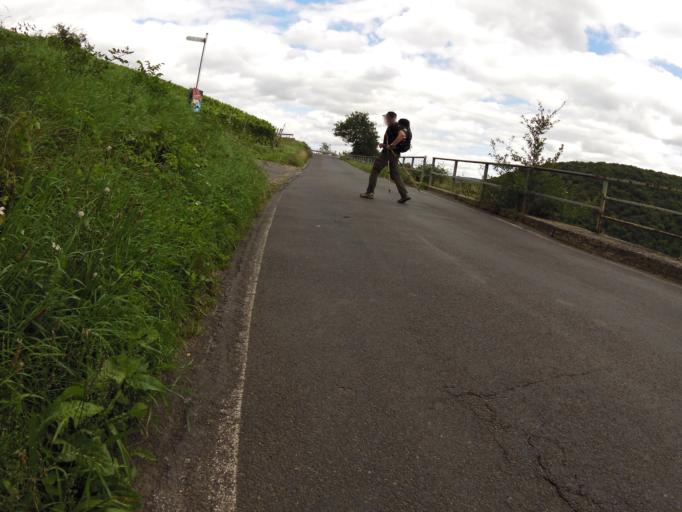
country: DE
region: Rheinland-Pfalz
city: Niederhausen
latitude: 49.8075
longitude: 7.7820
